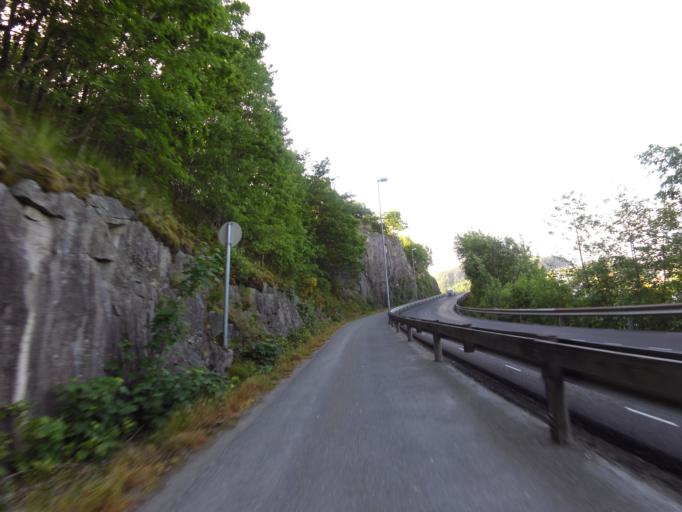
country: NO
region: Vest-Agder
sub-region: Flekkefjord
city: Flekkefjord
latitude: 58.2893
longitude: 6.6491
